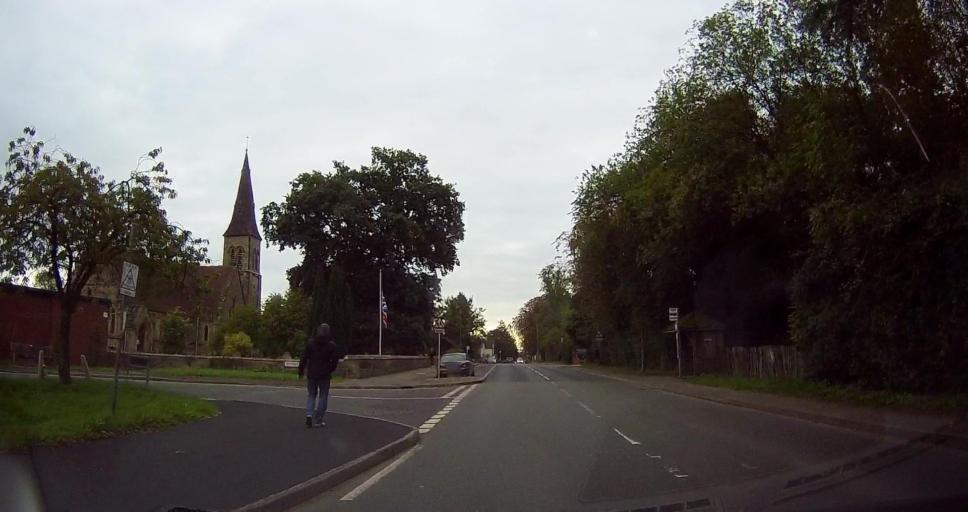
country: GB
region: England
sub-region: Kent
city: Tonbridge
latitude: 51.2175
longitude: 0.2377
